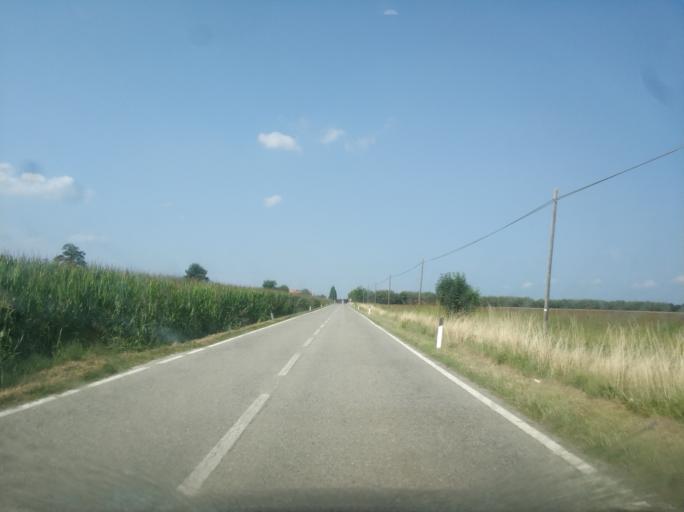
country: IT
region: Piedmont
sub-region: Provincia di Cuneo
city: Caraglio
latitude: 44.4458
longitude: 7.4546
